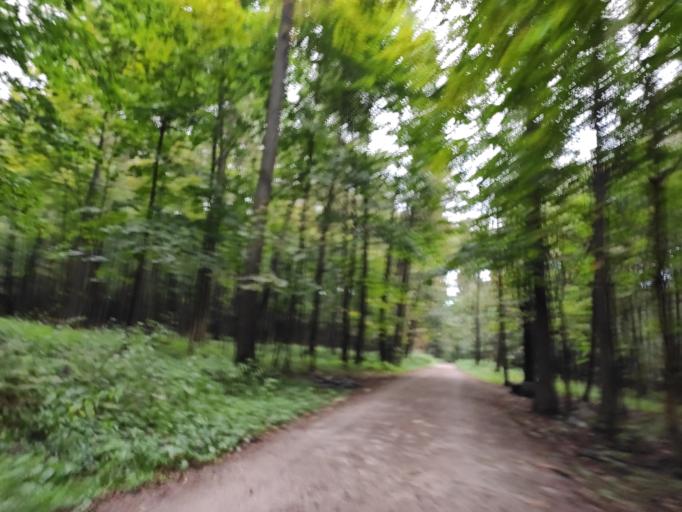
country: RU
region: Moskovskaya
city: Izmaylovo
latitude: 55.7700
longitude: 37.7893
